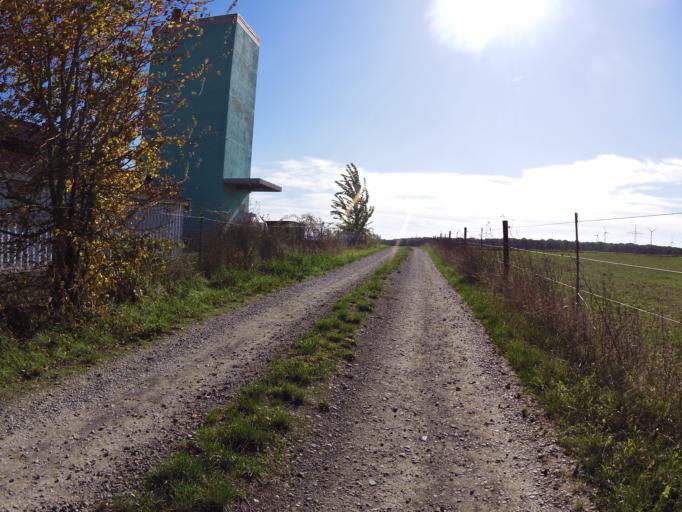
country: DE
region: Bavaria
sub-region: Regierungsbezirk Unterfranken
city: Theilheim
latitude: 49.7428
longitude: 10.0619
